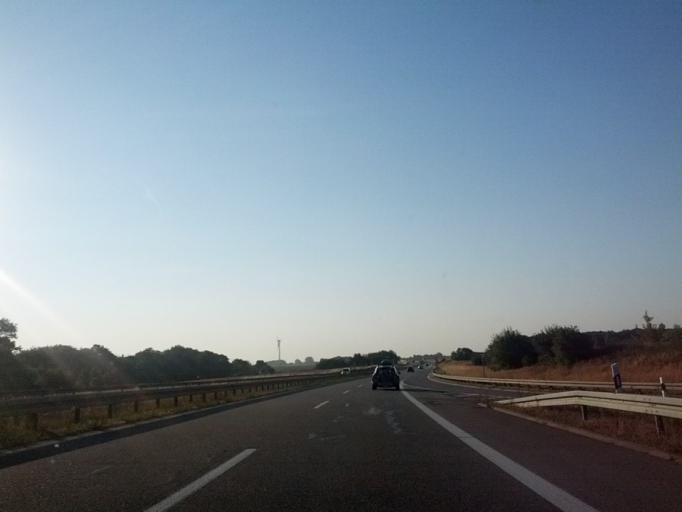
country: DE
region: Mecklenburg-Vorpommern
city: Zarrendorf
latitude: 54.2510
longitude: 13.1262
